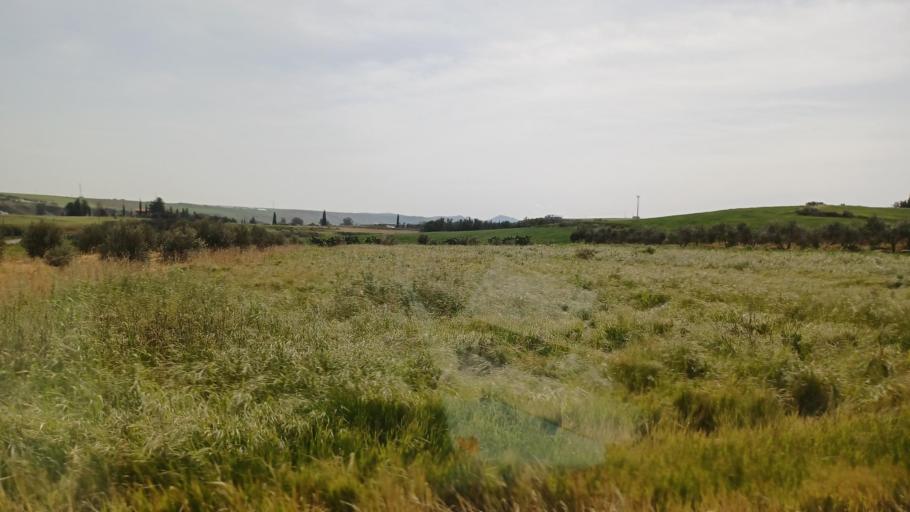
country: CY
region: Lefkosia
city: Astromeritis
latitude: 35.1063
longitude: 32.9668
